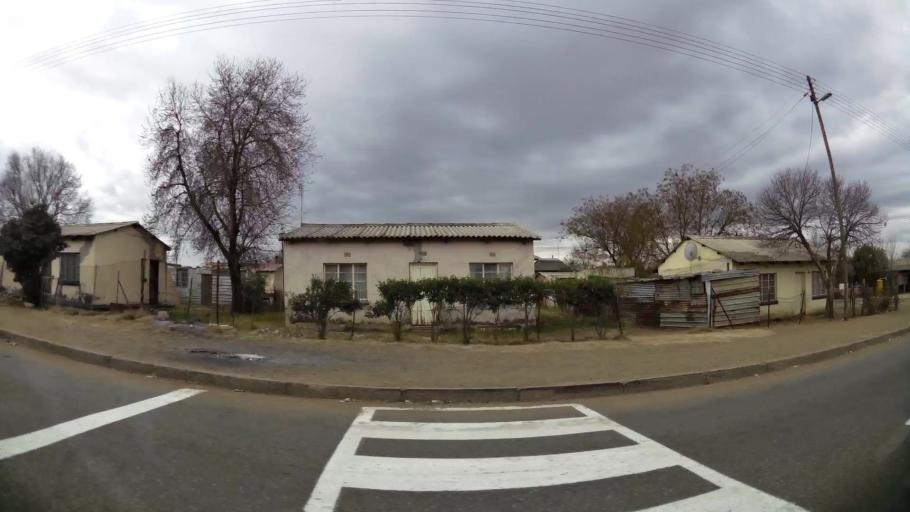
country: ZA
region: Orange Free State
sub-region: Fezile Dabi District Municipality
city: Kroonstad
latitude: -27.6523
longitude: 27.2085
